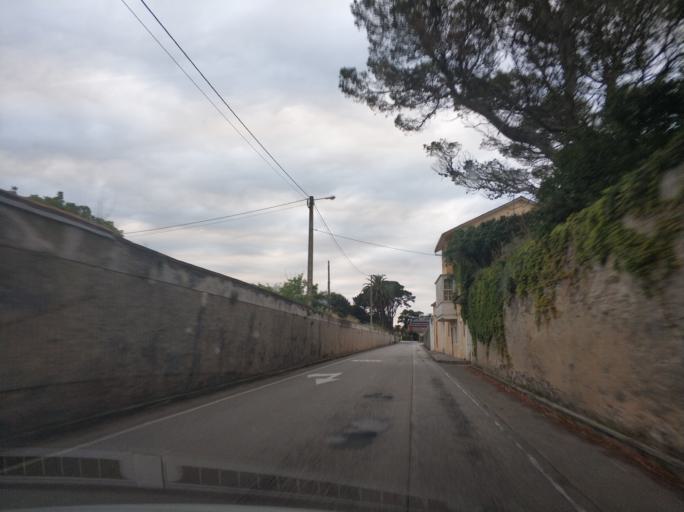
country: ES
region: Asturias
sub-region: Province of Asturias
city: Navia
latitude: 43.5430
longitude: -6.5252
